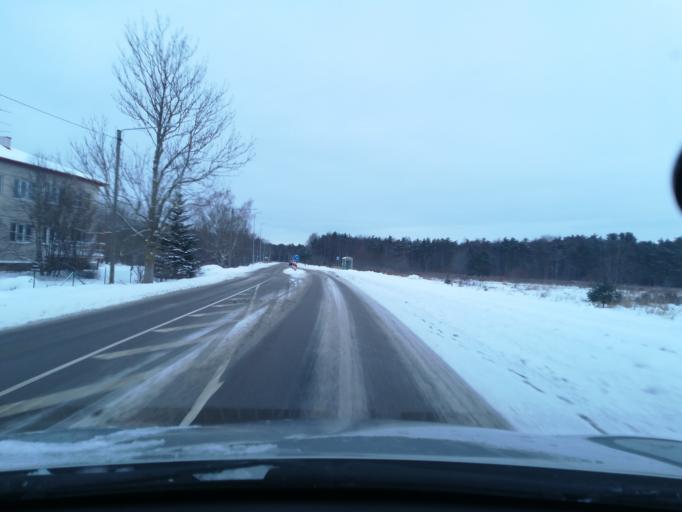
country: EE
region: Harju
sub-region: Keila linn
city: Keila
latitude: 59.3977
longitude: 24.3032
